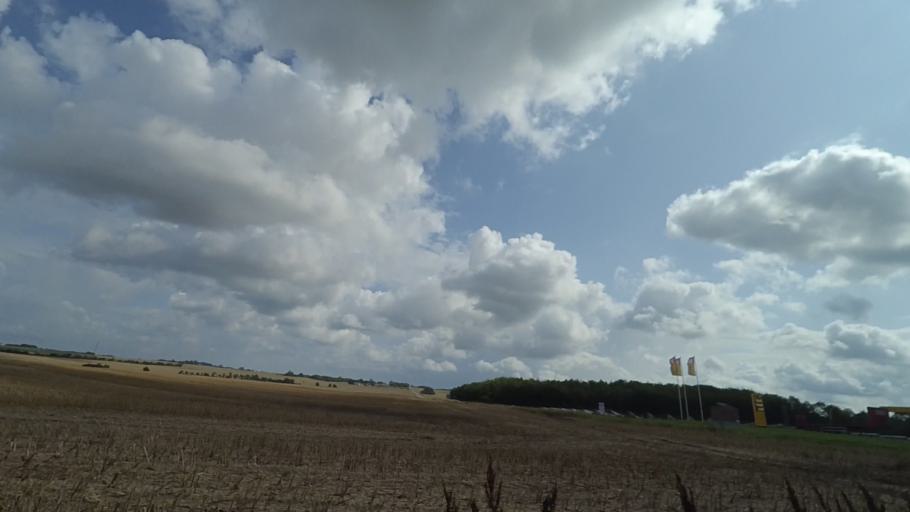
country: DK
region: Central Jutland
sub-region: Norddjurs Kommune
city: Auning
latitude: 56.4877
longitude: 10.4431
